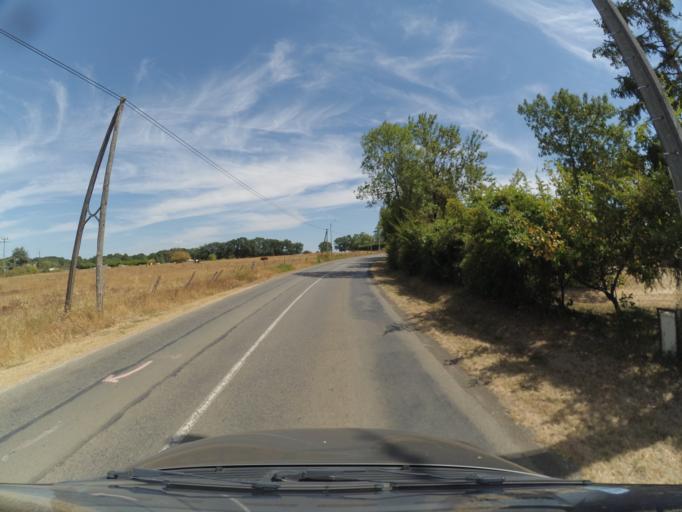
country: FR
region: Poitou-Charentes
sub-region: Departement de la Vienne
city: Vivonne
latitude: 46.4179
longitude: 0.3187
